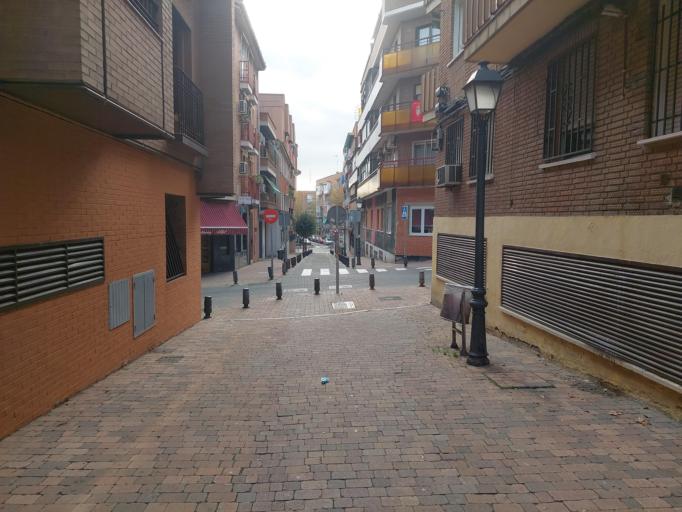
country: ES
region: Madrid
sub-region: Provincia de Madrid
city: Leganes
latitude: 40.3267
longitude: -3.7655
